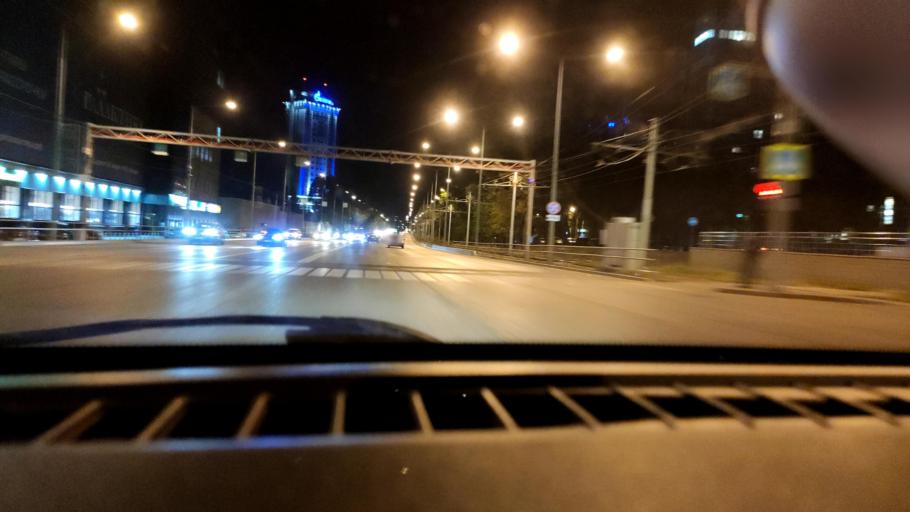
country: RU
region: Samara
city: Samara
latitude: 53.2170
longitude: 50.1479
